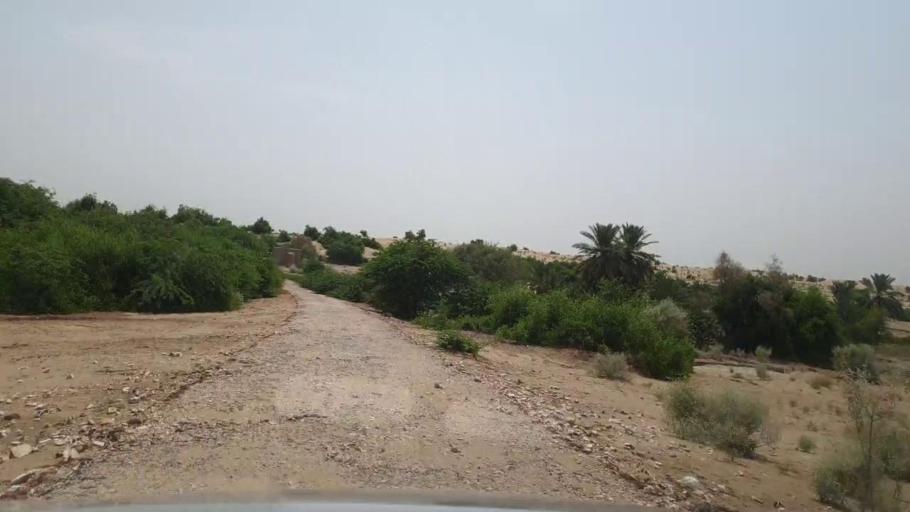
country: PK
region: Sindh
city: Pano Aqil
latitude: 27.5813
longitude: 69.1688
